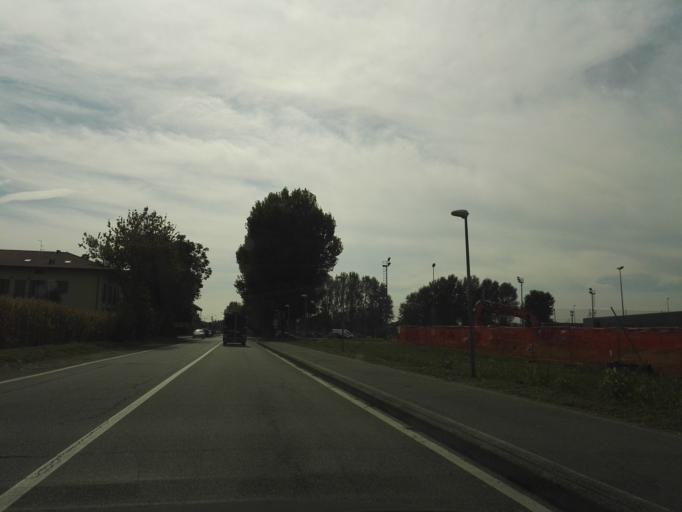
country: IT
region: Lombardy
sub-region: Citta metropolitana di Milano
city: Mezzate
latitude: 45.4340
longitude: 9.2939
